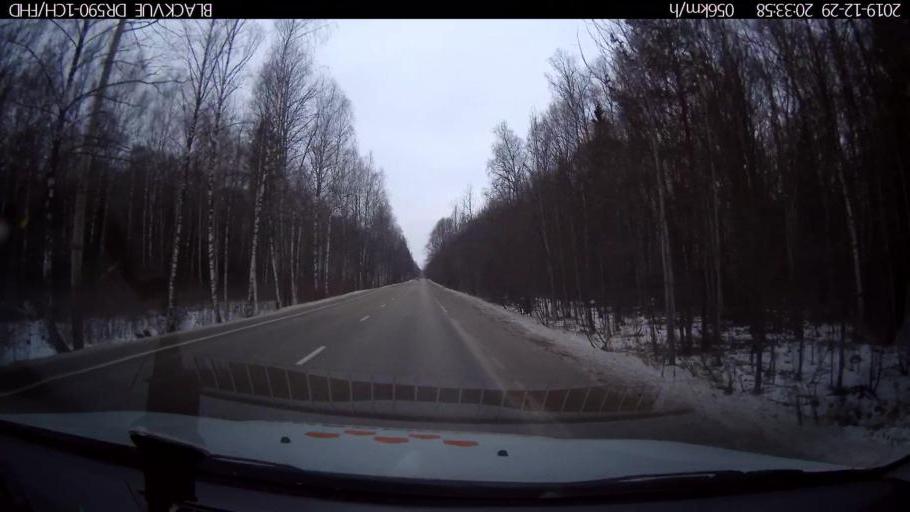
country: RU
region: Nizjnij Novgorod
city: Afonino
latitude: 56.1834
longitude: 44.0455
